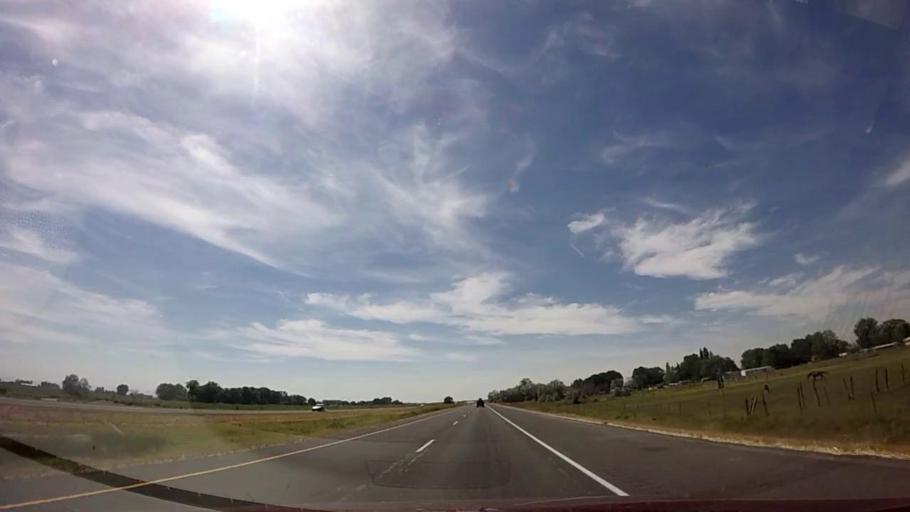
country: US
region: Idaho
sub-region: Minidoka County
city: Rupert
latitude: 42.5690
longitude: -113.6906
